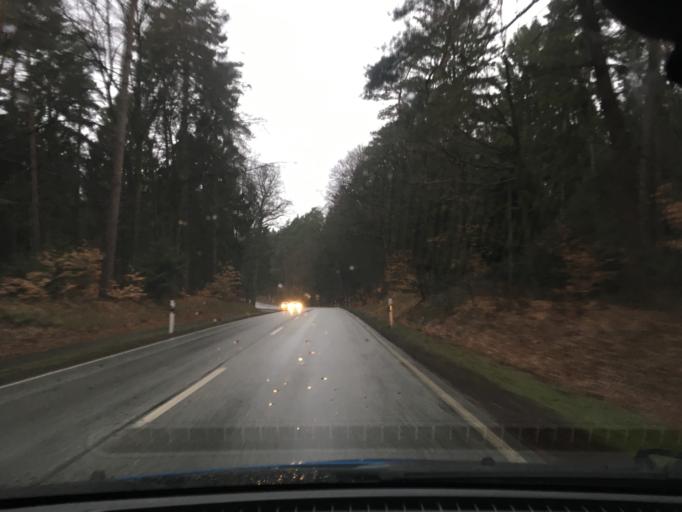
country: DE
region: Schleswig-Holstein
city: Krukow
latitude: 53.3996
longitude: 10.4606
